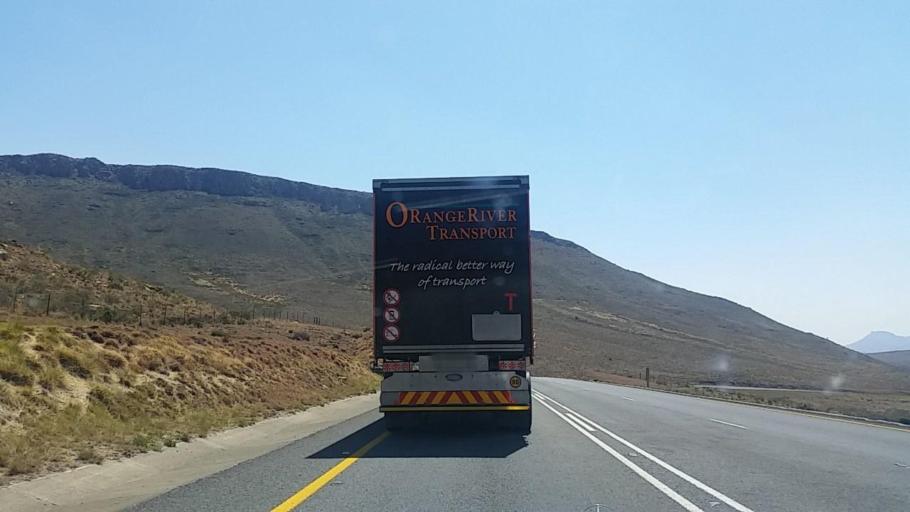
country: ZA
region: Eastern Cape
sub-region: Chris Hani District Municipality
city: Middelburg
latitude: -31.8218
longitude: 24.8566
